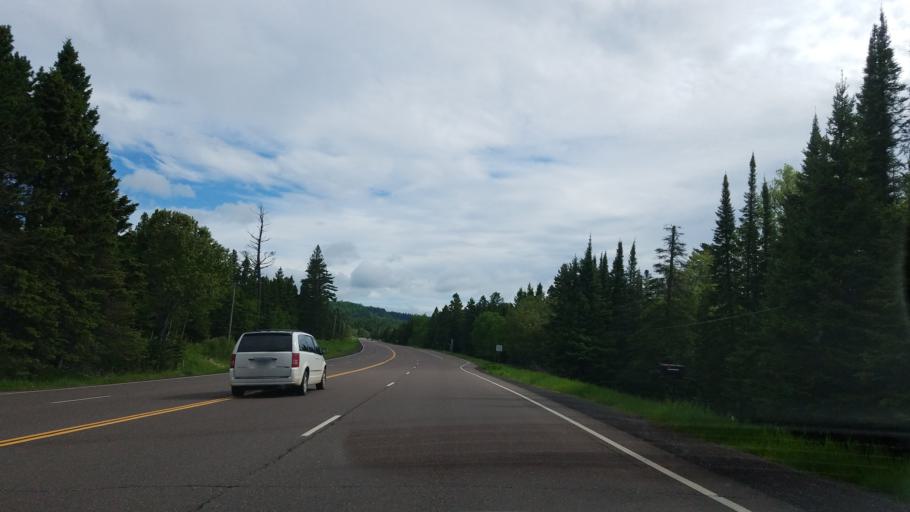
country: US
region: Minnesota
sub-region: Lake County
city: Two Harbors
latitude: 47.0844
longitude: -91.5813
